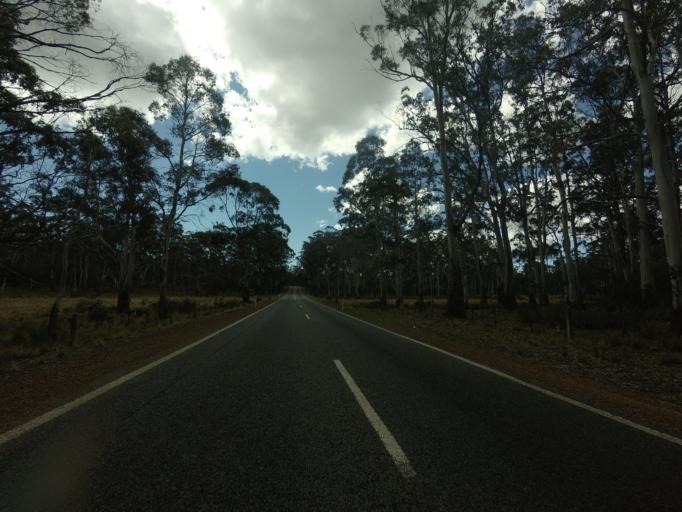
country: AU
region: Tasmania
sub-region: Northern Midlands
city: Evandale
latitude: -41.9685
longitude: 147.6452
